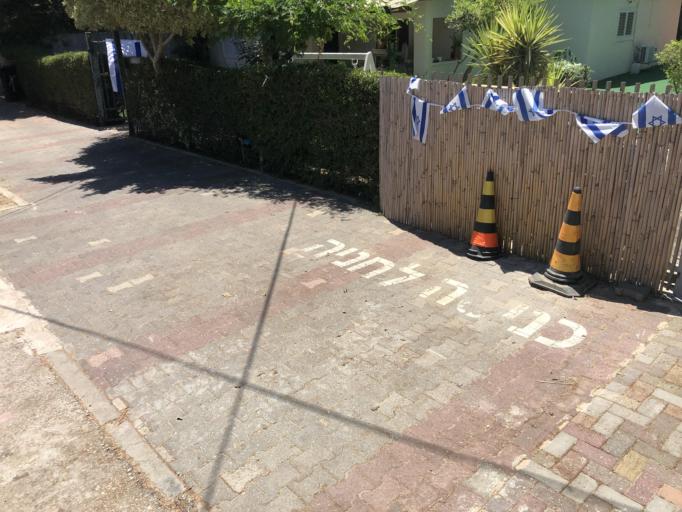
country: IL
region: Tel Aviv
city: Or Yehuda
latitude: 32.0288
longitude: 34.8723
